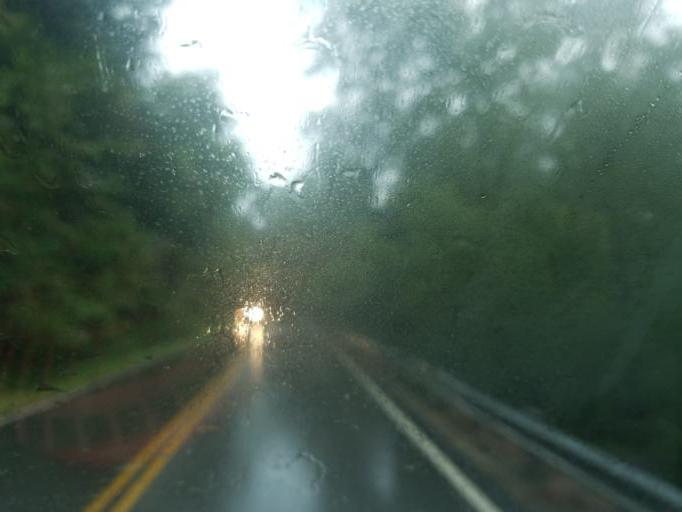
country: US
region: Kentucky
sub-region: Carter County
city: Grayson
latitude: 38.4943
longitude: -82.9769
